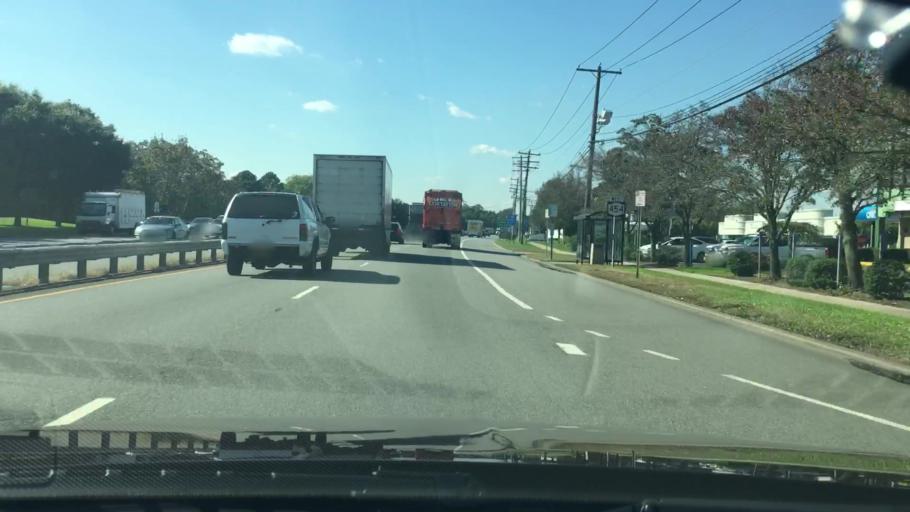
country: US
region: New York
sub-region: Suffolk County
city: Bohemia
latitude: 40.7826
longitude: -73.0984
